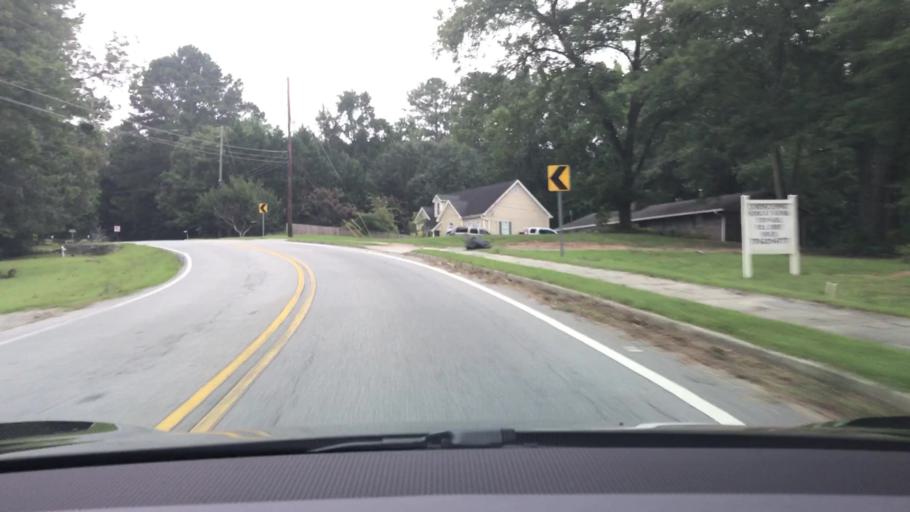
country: US
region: Georgia
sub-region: Gwinnett County
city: Suwanee
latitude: 34.0828
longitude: -84.0657
